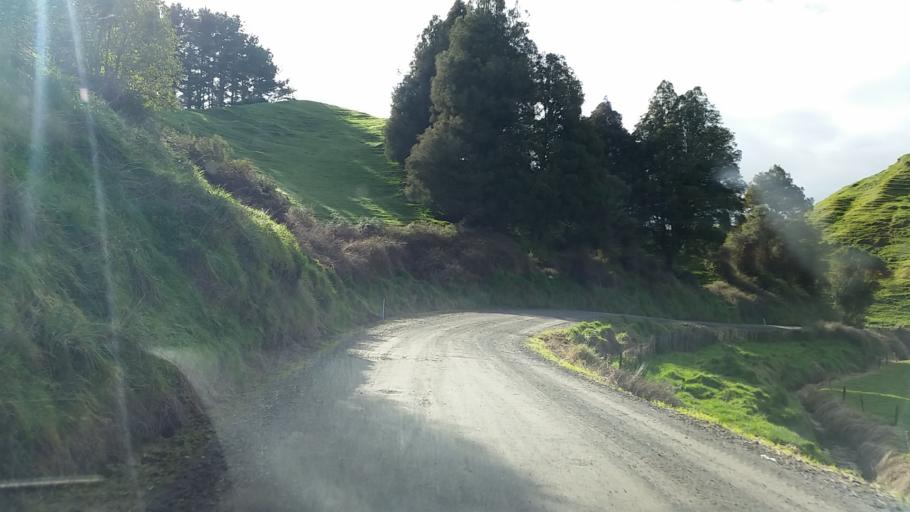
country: NZ
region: Taranaki
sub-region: South Taranaki District
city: Eltham
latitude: -39.2564
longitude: 174.5110
